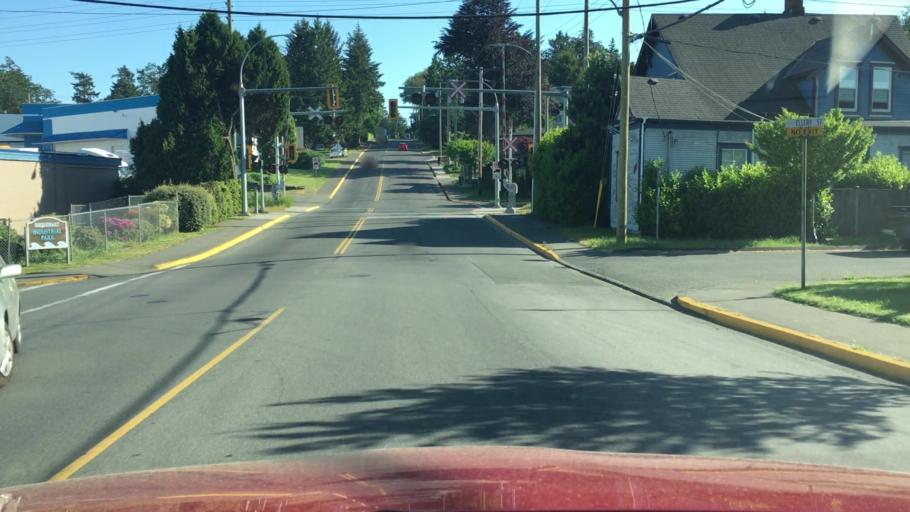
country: CA
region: British Columbia
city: Victoria
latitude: 48.4374
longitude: -123.4024
